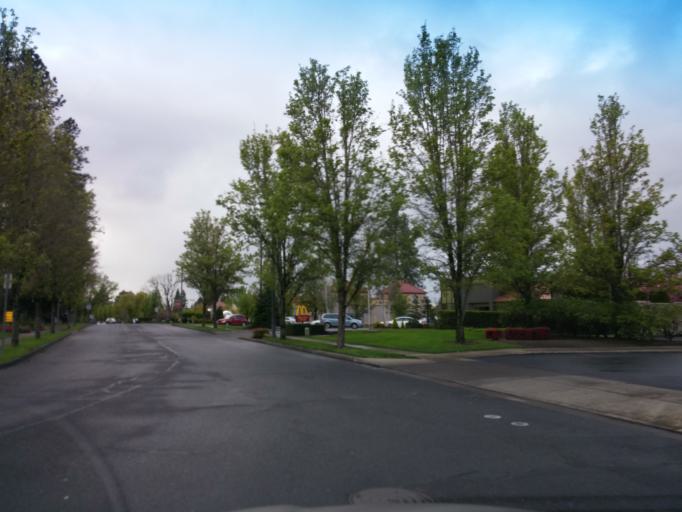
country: US
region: Oregon
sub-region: Washington County
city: Oak Hills
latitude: 45.5163
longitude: -122.8411
